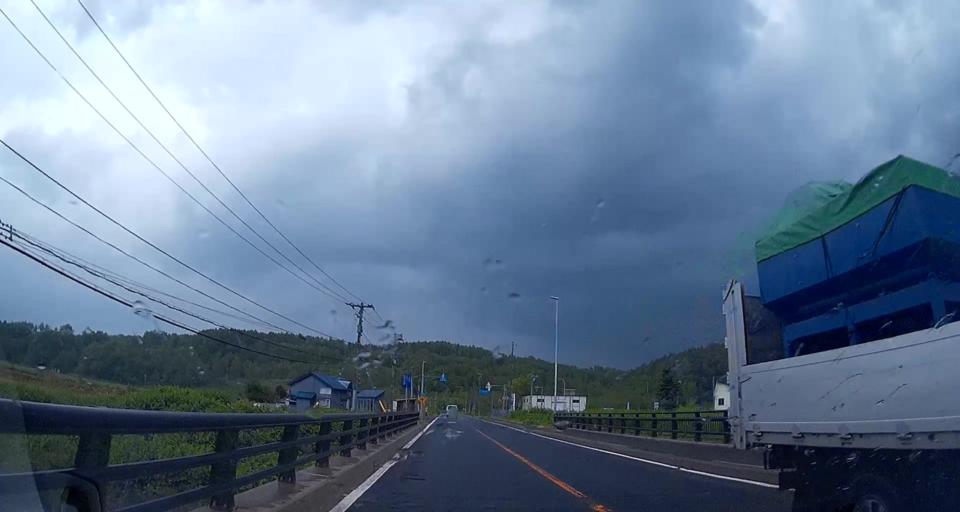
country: JP
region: Hokkaido
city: Niseko Town
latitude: 42.8785
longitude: 140.8823
